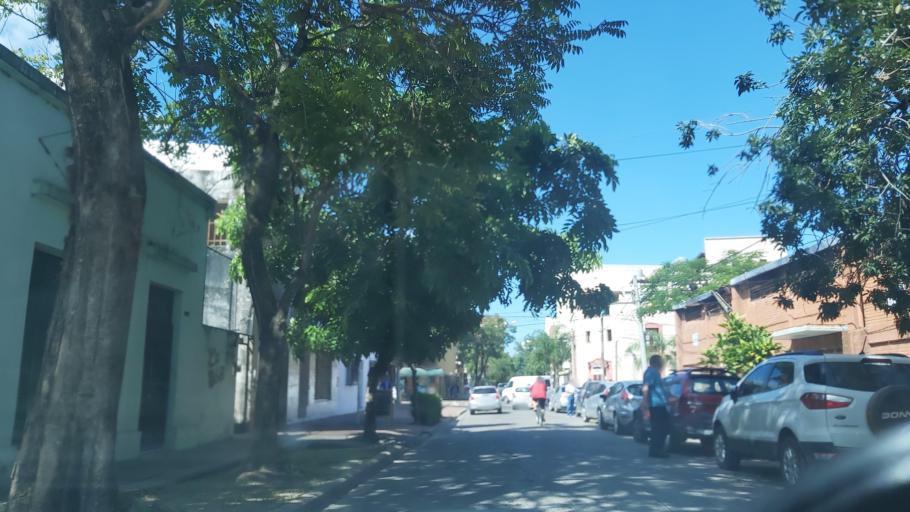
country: AR
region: Corrientes
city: Corrientes
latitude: -27.4767
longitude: -58.8353
